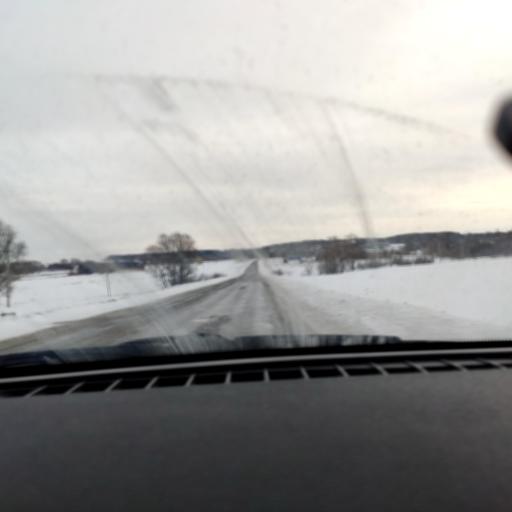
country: RU
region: Bashkortostan
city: Iglino
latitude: 54.7816
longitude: 56.5376
